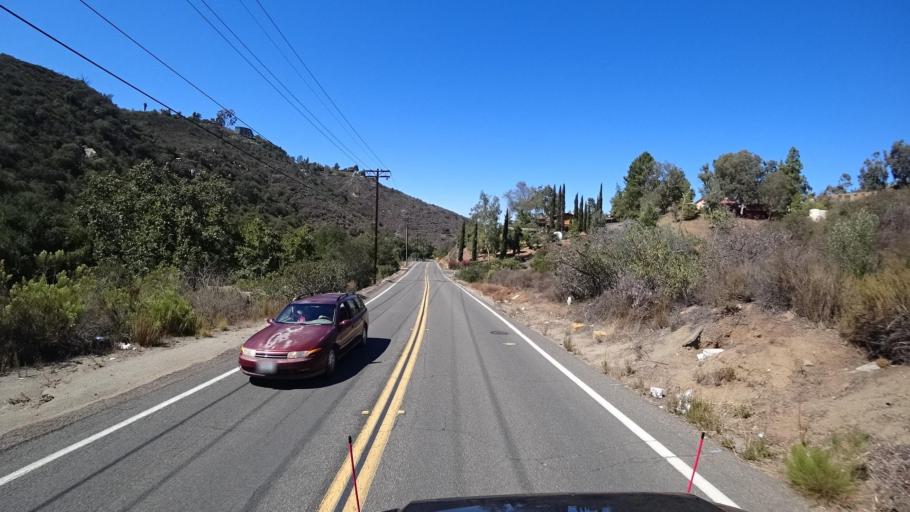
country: US
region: California
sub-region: San Diego County
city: Jamul
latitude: 32.7303
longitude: -116.8746
